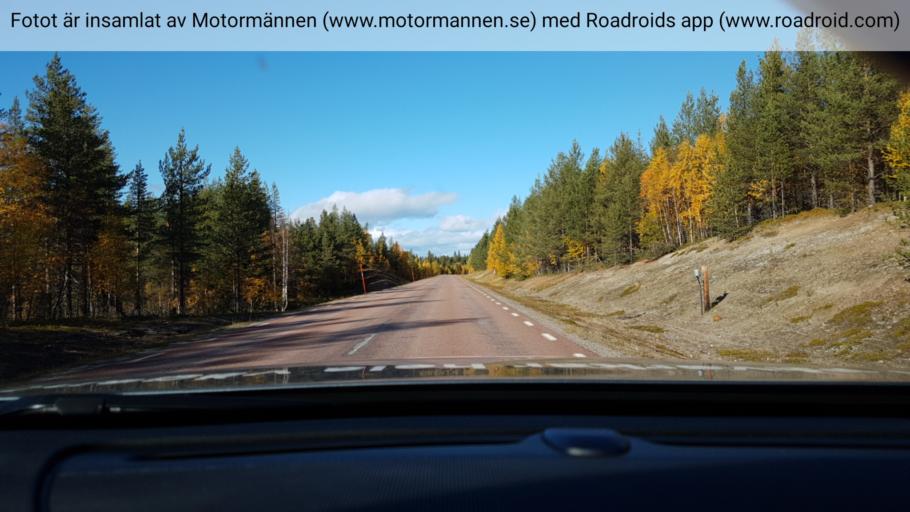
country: SE
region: Norrbotten
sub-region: Arjeplogs Kommun
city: Arjeplog
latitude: 66.0101
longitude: 18.0957
